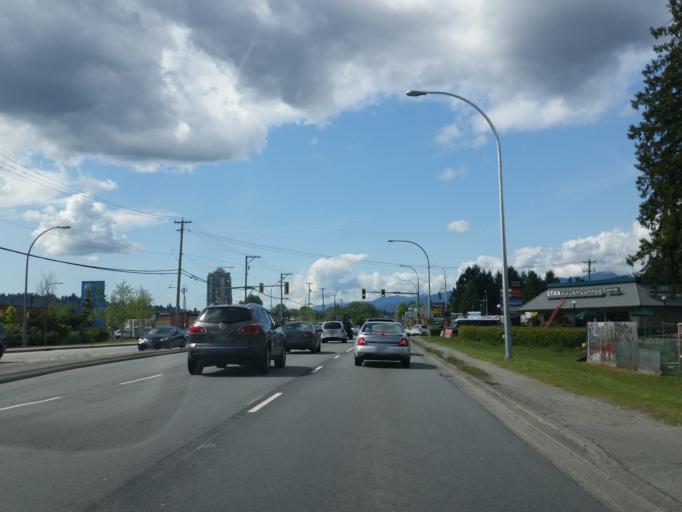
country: CA
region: British Columbia
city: Coquitlam
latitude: 49.2633
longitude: -122.7660
